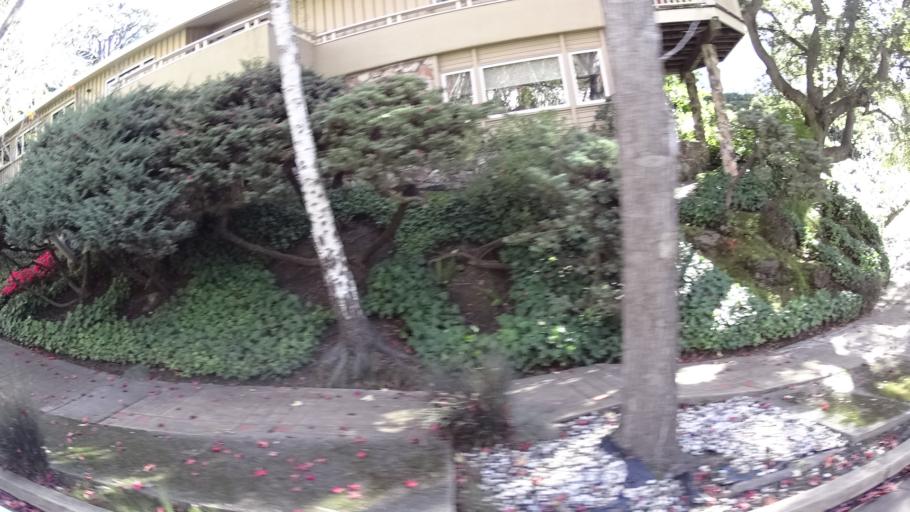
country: US
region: California
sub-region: Alameda County
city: Piedmont
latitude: 37.8156
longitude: -122.2158
